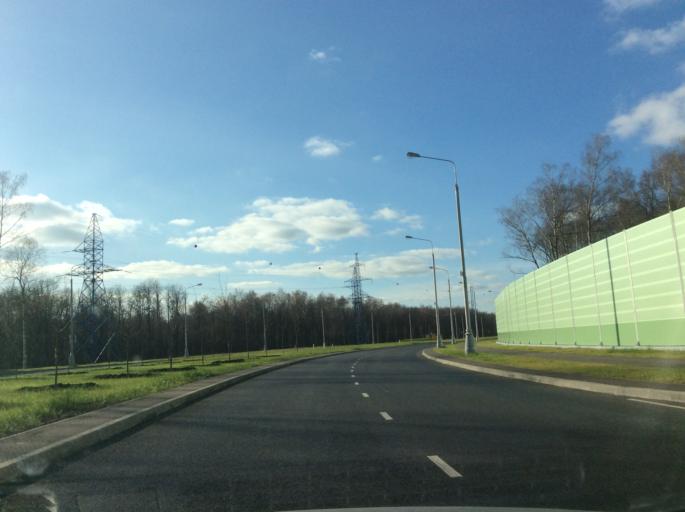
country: RU
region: Moskovskaya
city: Vatutinki
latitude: 55.4825
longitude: 37.3712
